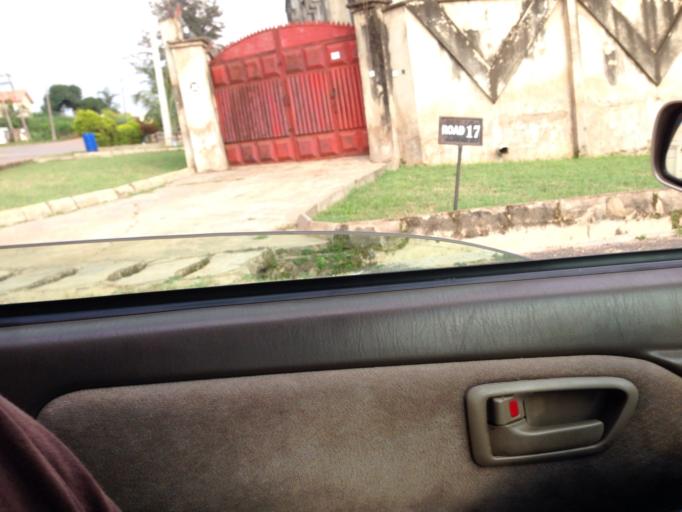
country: NG
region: Oyo
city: Ibadan
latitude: 7.4280
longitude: 3.9441
